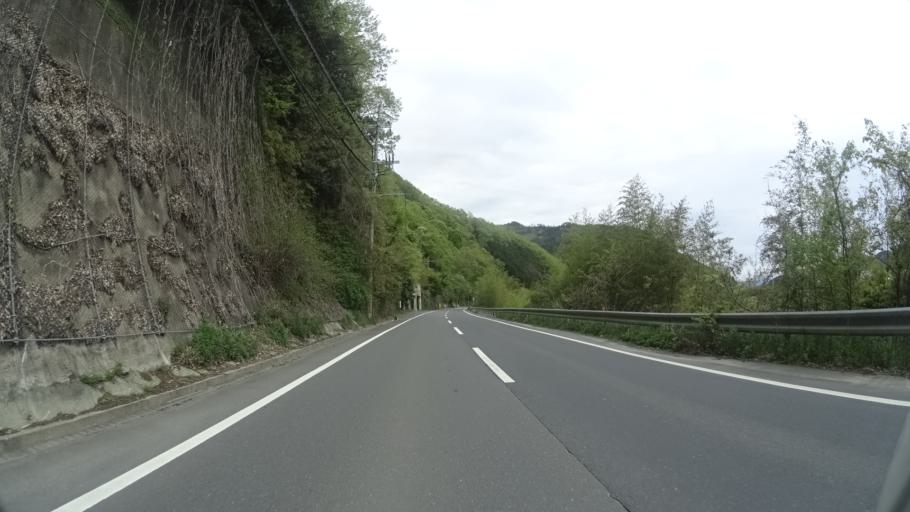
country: JP
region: Kyoto
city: Kameoka
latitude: 35.1193
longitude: 135.5124
